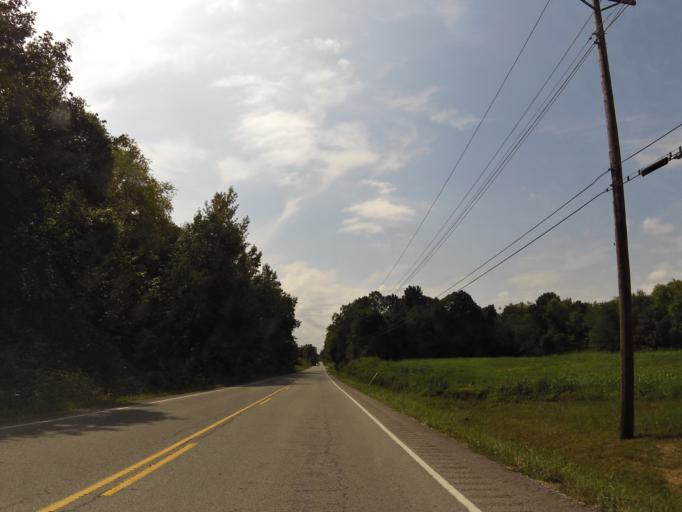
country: US
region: Tennessee
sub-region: Humphreys County
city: Waverly
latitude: 35.8620
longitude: -87.8094
